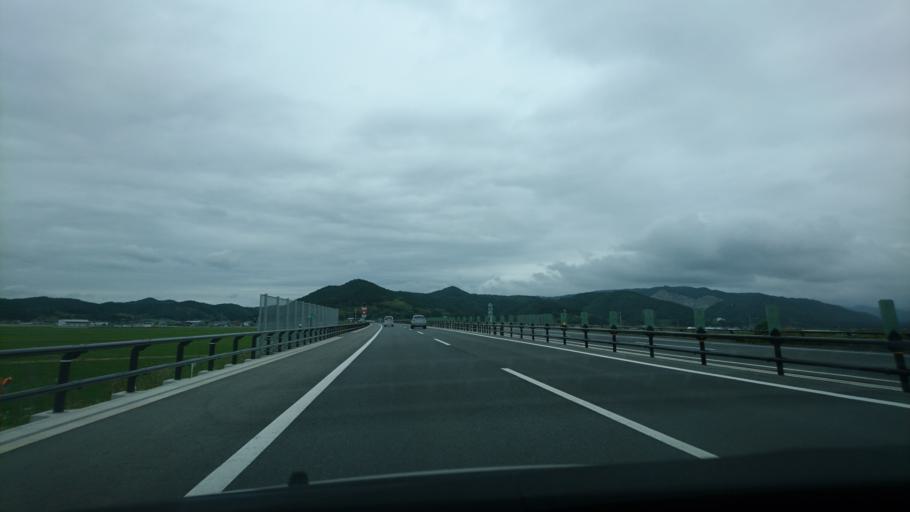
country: JP
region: Miyagi
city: Ishinomaki
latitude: 38.5130
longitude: 141.2878
